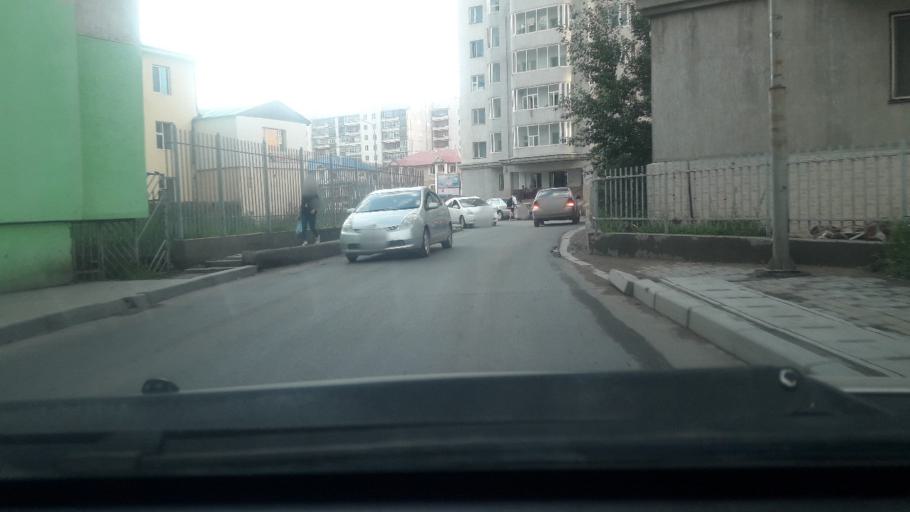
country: MN
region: Ulaanbaatar
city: Ulaanbaatar
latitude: 47.9115
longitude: 106.9340
